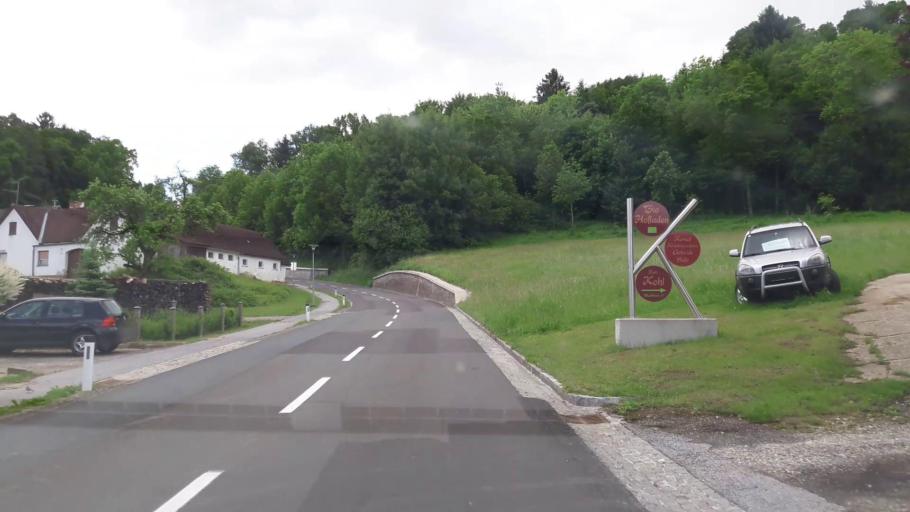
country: AT
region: Styria
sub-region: Politischer Bezirk Hartberg-Fuerstenfeld
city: Soechau
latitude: 47.0594
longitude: 16.0085
